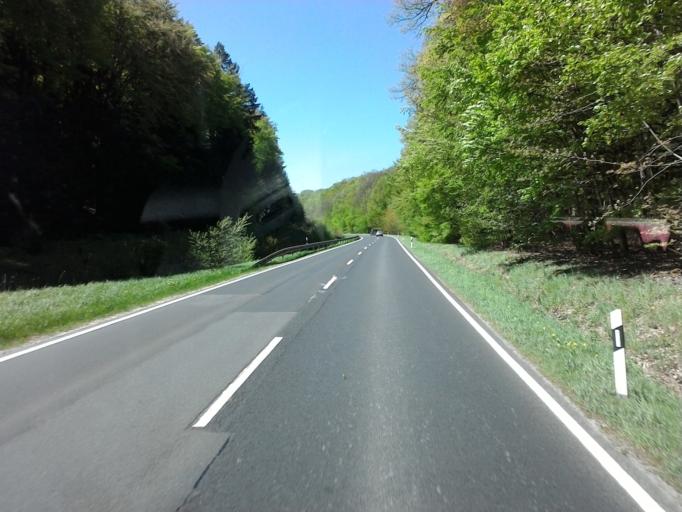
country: DE
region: Bavaria
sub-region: Regierungsbezirk Unterfranken
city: Rechtenbach
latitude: 49.9822
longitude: 9.4790
